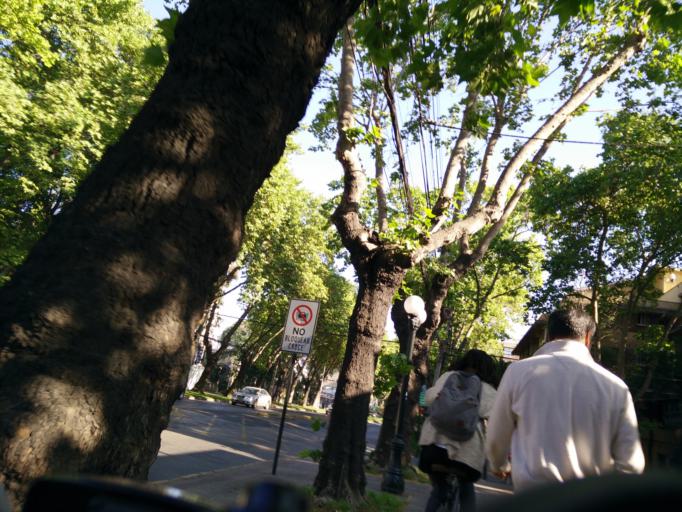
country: CL
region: Santiago Metropolitan
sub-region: Provincia de Santiago
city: Villa Presidente Frei, Nunoa, Santiago, Chile
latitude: -33.4439
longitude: -70.6063
